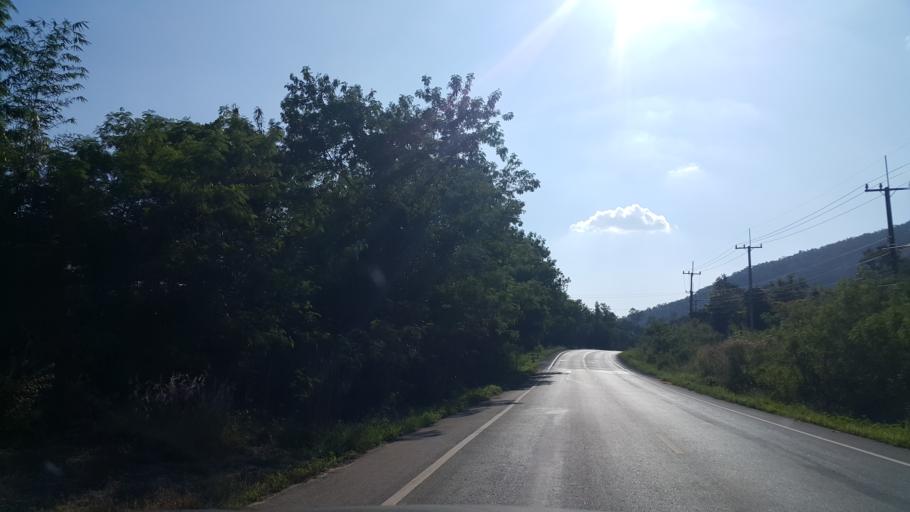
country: TH
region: Lamphun
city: Mae Tha
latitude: 18.4929
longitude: 99.1906
